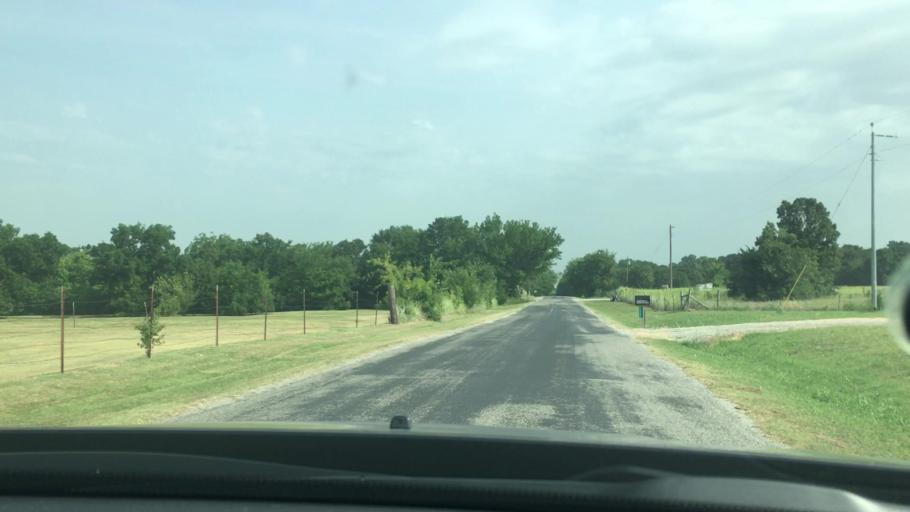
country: US
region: Oklahoma
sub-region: Garvin County
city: Pauls Valley
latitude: 34.8065
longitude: -97.1955
